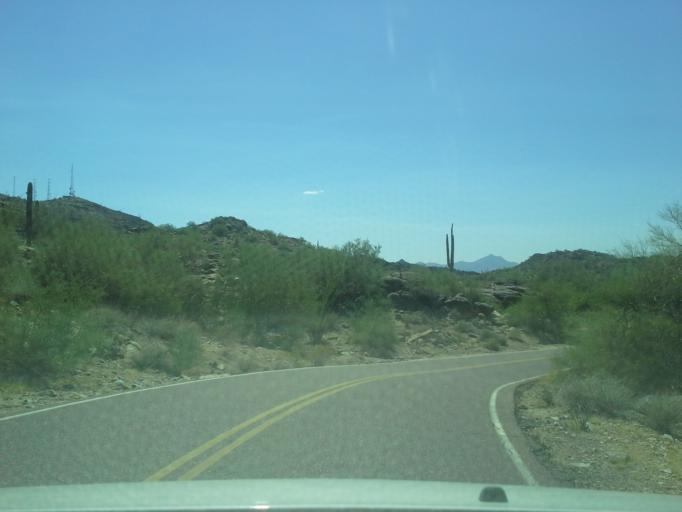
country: US
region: Arizona
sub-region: Maricopa County
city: Guadalupe
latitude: 33.3418
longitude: -112.0592
